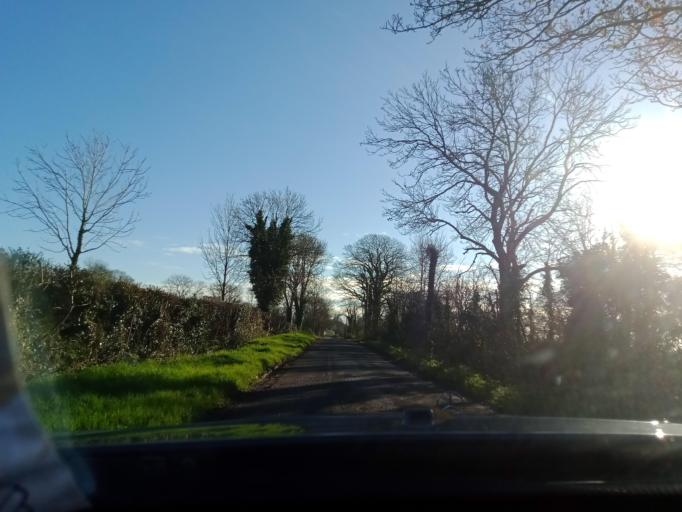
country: IE
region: Leinster
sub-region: Kilkenny
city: Mooncoin
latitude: 52.3409
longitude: -7.2700
